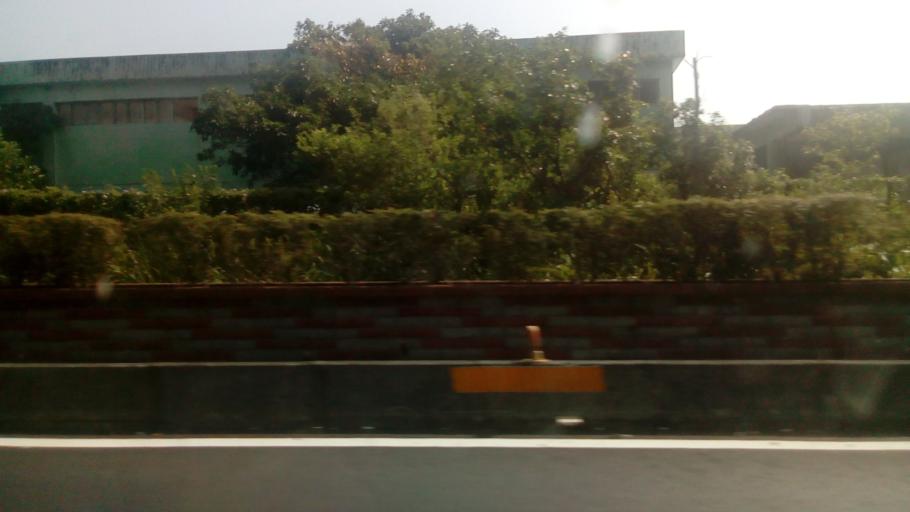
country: TW
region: Taiwan
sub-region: Yilan
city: Yilan
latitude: 24.5868
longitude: 121.8644
